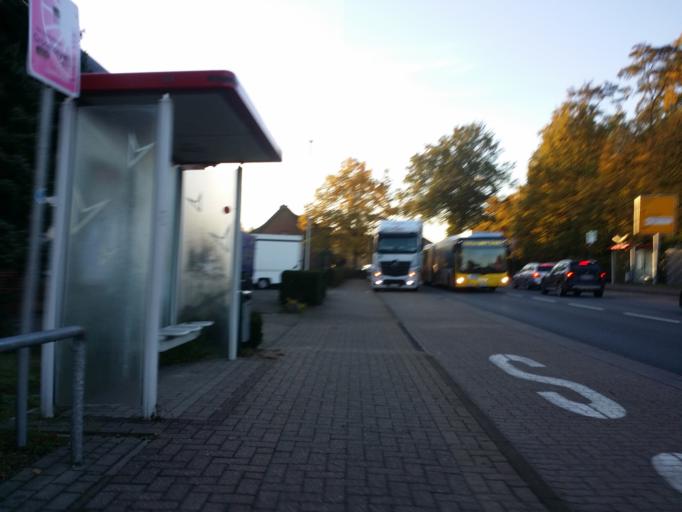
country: DE
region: Lower Saxony
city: Kirchseelte
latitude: 52.9993
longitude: 8.7050
